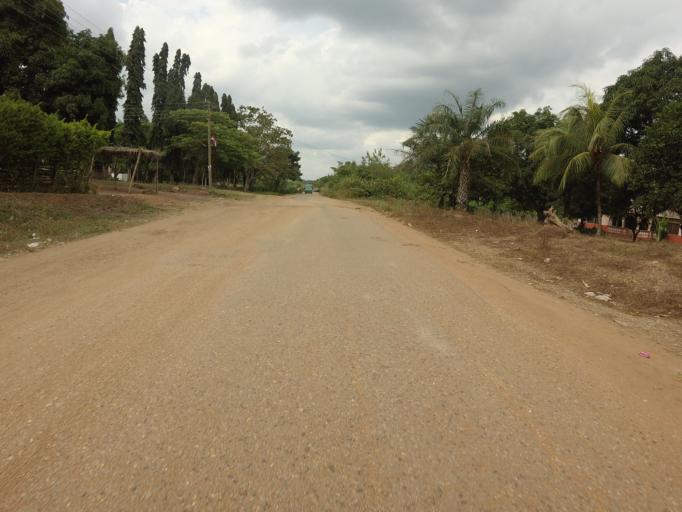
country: GH
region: Volta
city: Ho
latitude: 6.6555
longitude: 0.3448
